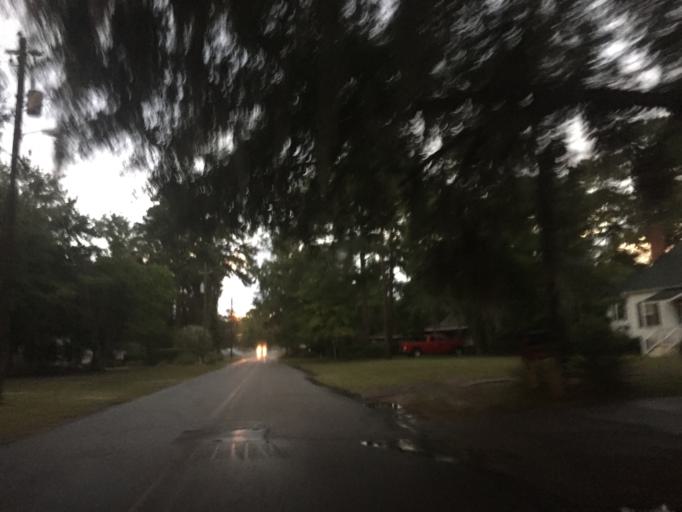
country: US
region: Georgia
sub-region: Liberty County
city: Hinesville
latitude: 31.8438
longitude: -81.5961
